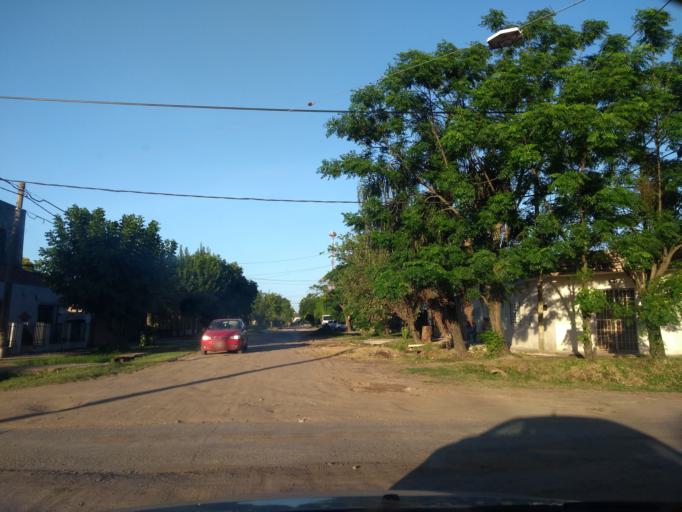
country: AR
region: Chaco
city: Barranqueras
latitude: -27.4855
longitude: -58.9443
